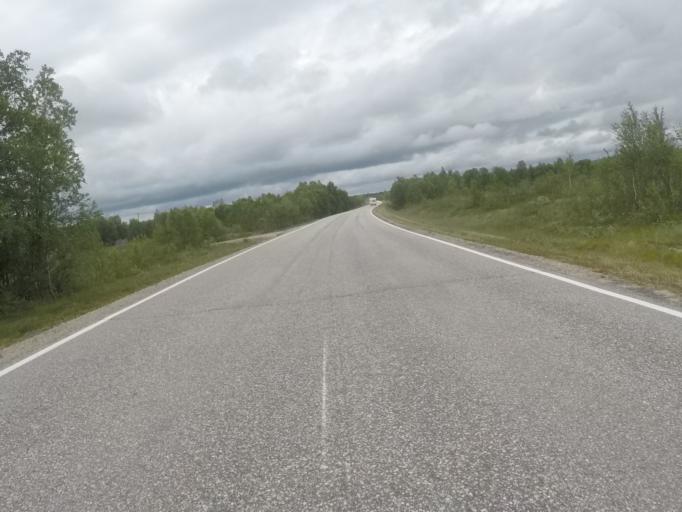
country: FI
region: Lapland
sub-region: Tunturi-Lappi
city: Enontekioe
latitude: 68.4836
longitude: 23.3594
